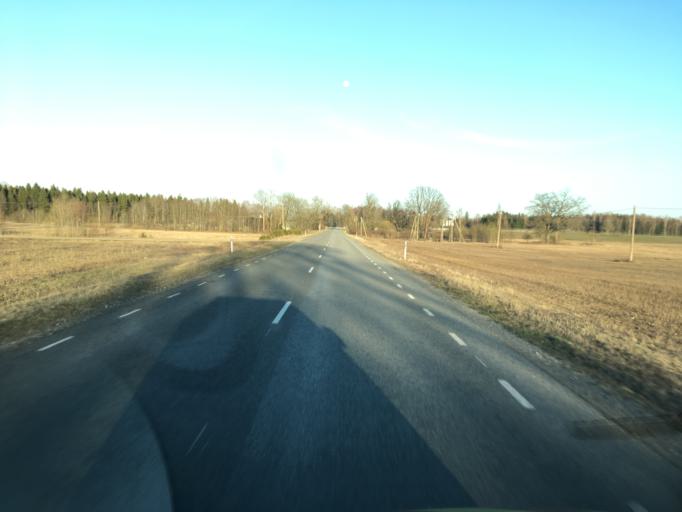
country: EE
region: Raplamaa
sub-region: Rapla vald
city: Rapla
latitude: 59.0772
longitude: 24.8647
